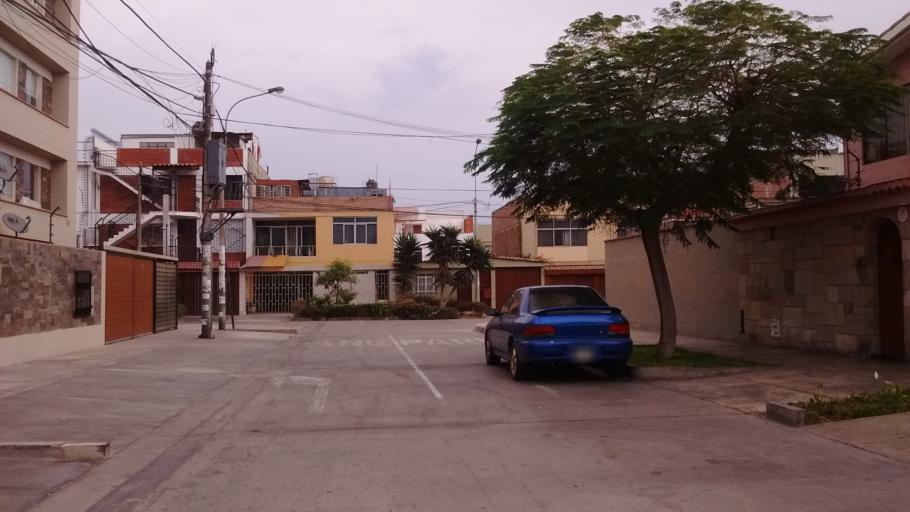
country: PE
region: Lima
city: Lima
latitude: -12.0668
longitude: -77.0680
